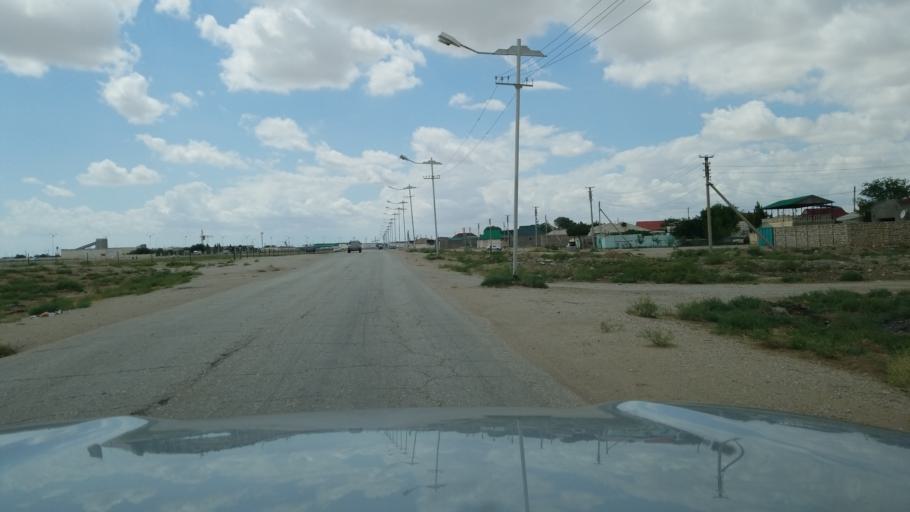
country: TM
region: Balkan
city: Balkanabat
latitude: 39.4916
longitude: 54.3887
